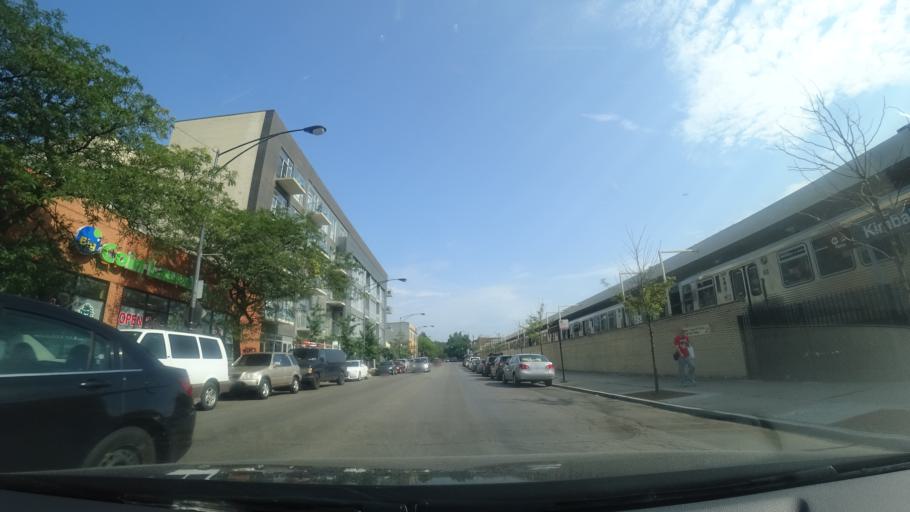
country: US
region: Illinois
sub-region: Cook County
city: Lincolnwood
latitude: 41.9670
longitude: -87.7133
